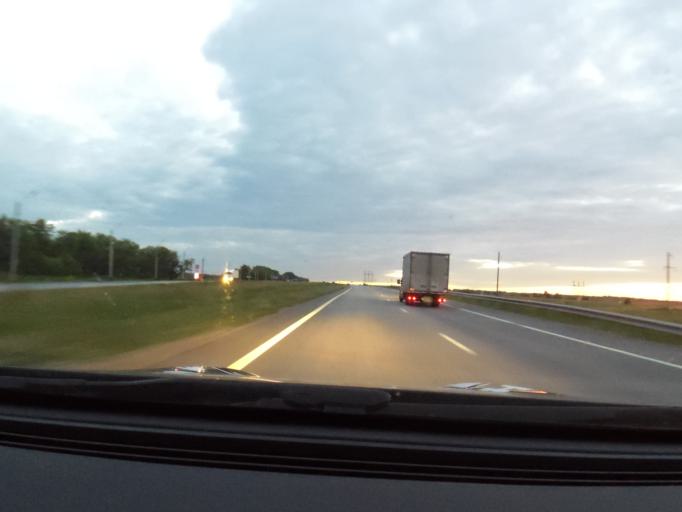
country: RU
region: Chuvashia
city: Yadrin
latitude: 55.9995
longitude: 46.0961
